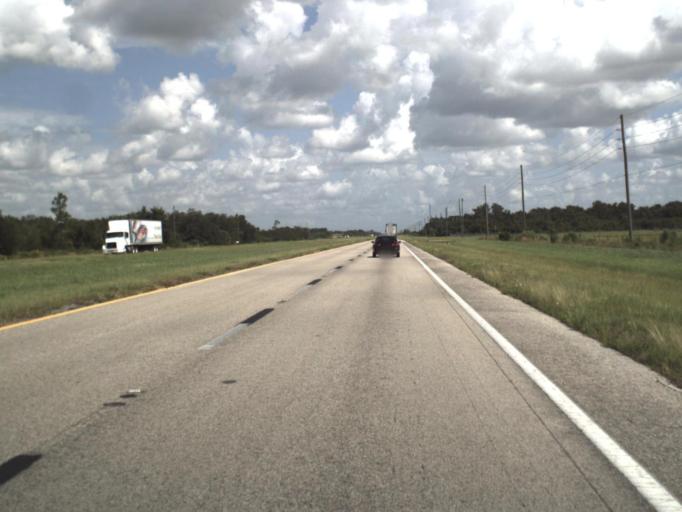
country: US
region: Florida
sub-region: Charlotte County
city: Harbour Heights
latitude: 27.0186
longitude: -81.9584
